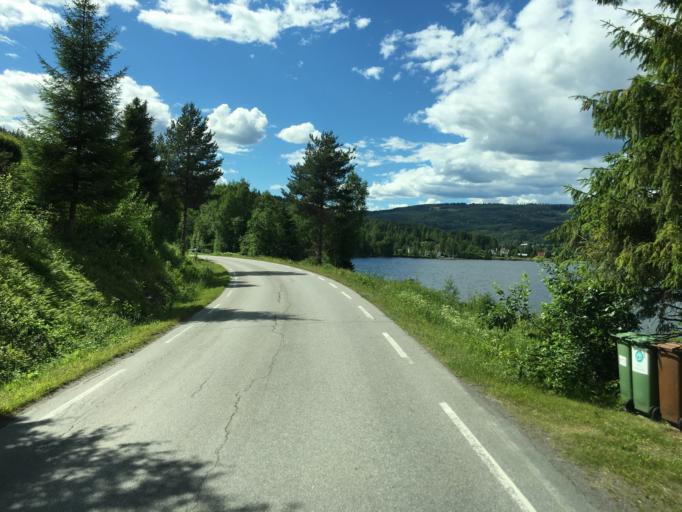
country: NO
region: Oppland
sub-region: Sondre Land
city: Hov
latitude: 60.5128
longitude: 10.3148
